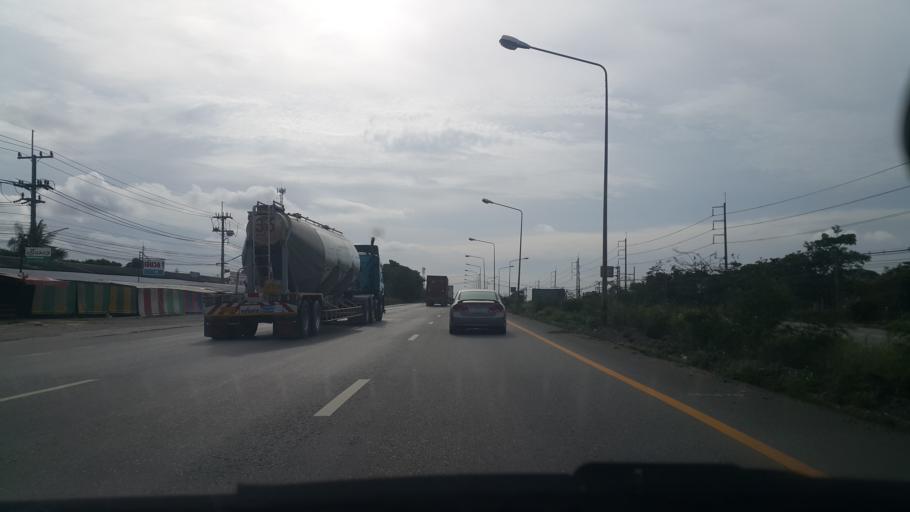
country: TH
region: Rayong
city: Nikhom Phattana
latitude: 12.8641
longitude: 101.0777
